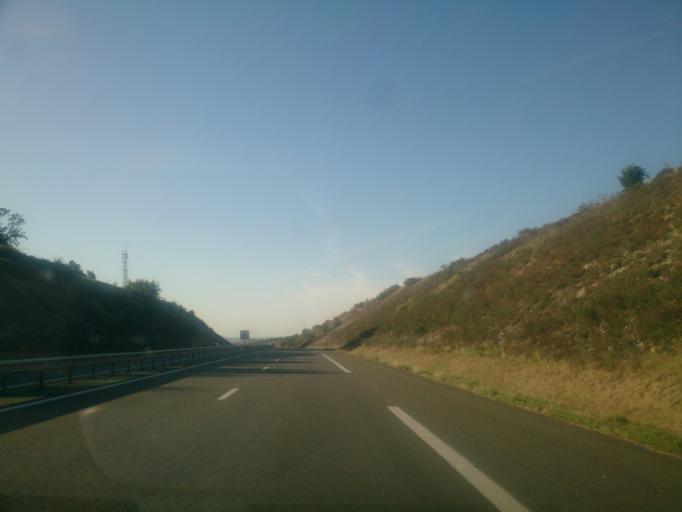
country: FR
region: Midi-Pyrenees
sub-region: Departement du Lot
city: Le Vigan
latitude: 44.7100
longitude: 1.5712
